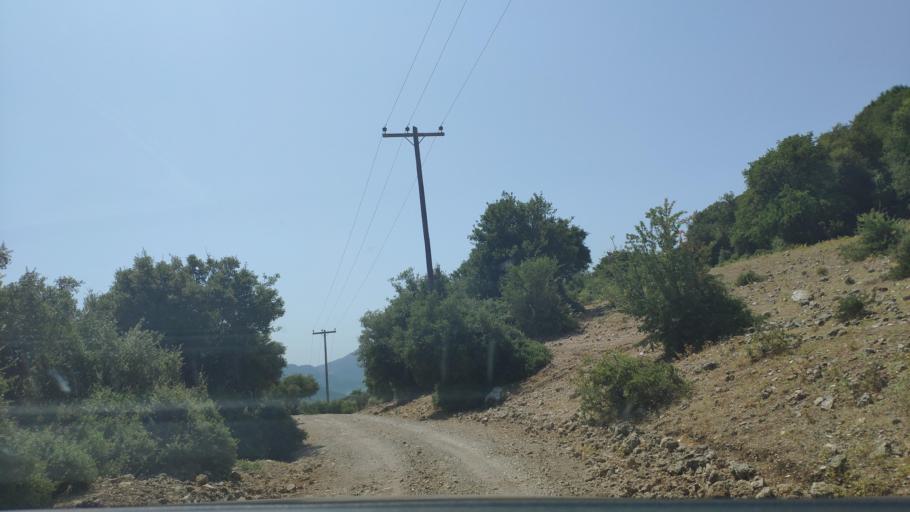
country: GR
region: West Greece
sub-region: Nomos Aitolias kai Akarnanias
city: Monastirakion
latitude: 38.8154
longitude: 21.0255
